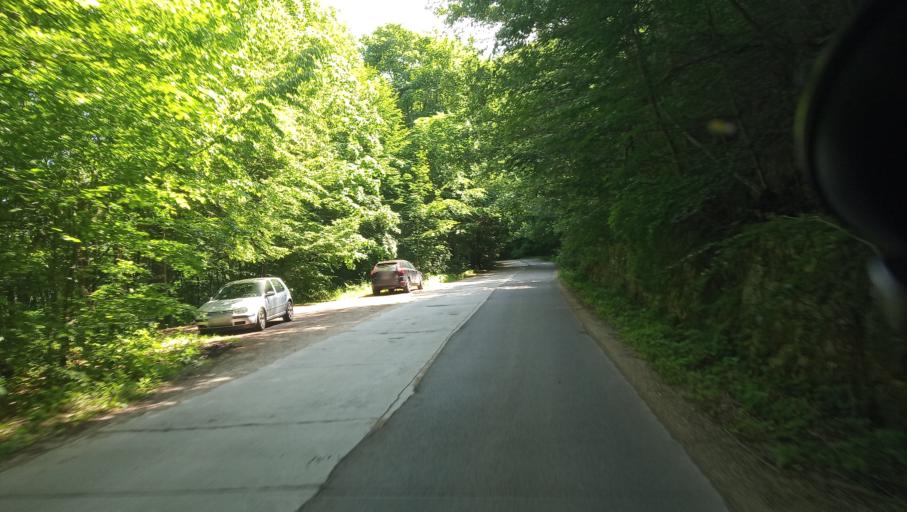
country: RO
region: Cluj
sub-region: Comuna Capusu Mare
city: Capusu Mare
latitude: 46.7096
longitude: 23.2626
